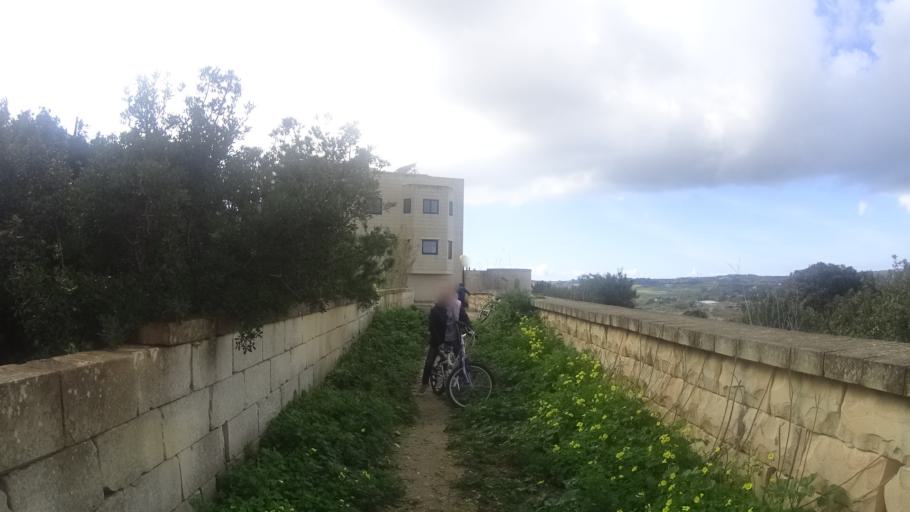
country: MT
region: L-Imtarfa
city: Imtarfa
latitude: 35.8907
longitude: 14.3935
